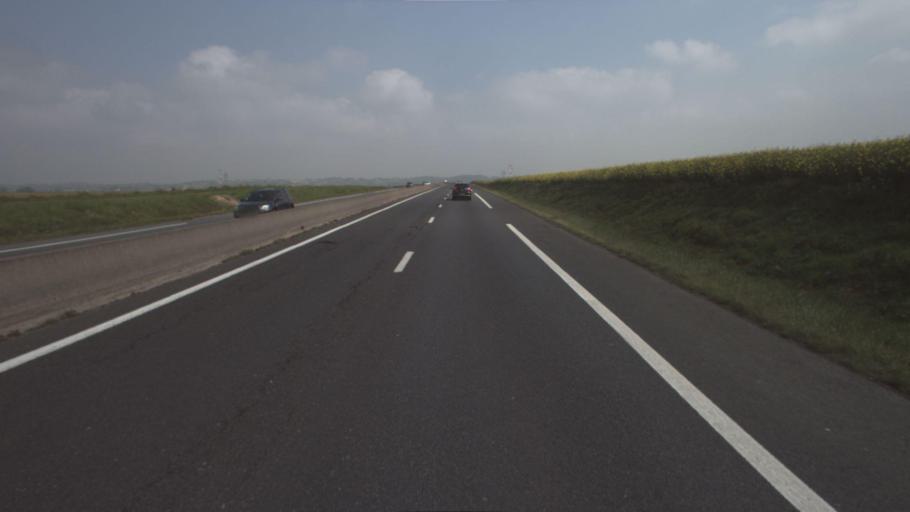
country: FR
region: Ile-de-France
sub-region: Departement de Seine-et-Marne
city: Longperrier
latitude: 49.0237
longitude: 2.6663
